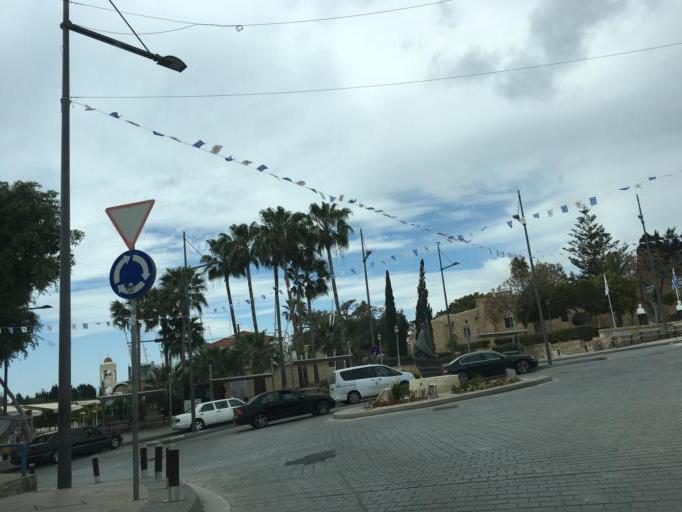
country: CY
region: Ammochostos
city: Ayia Napa
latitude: 34.9887
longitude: 34.0005
